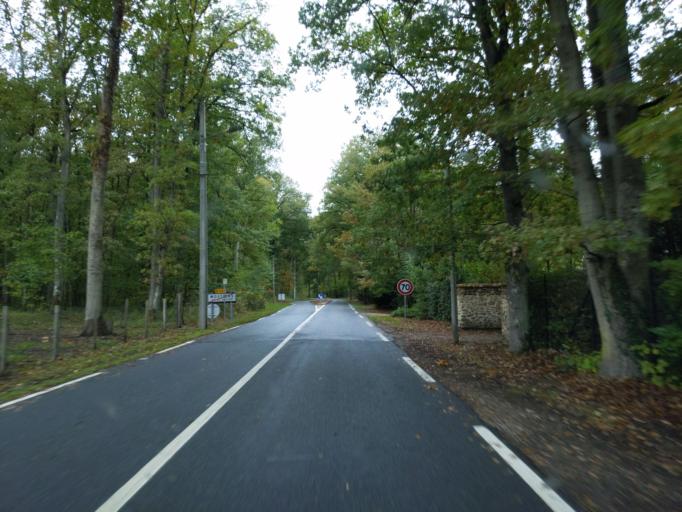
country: FR
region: Ile-de-France
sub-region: Departement des Yvelines
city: Bullion
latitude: 48.6108
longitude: 1.9668
